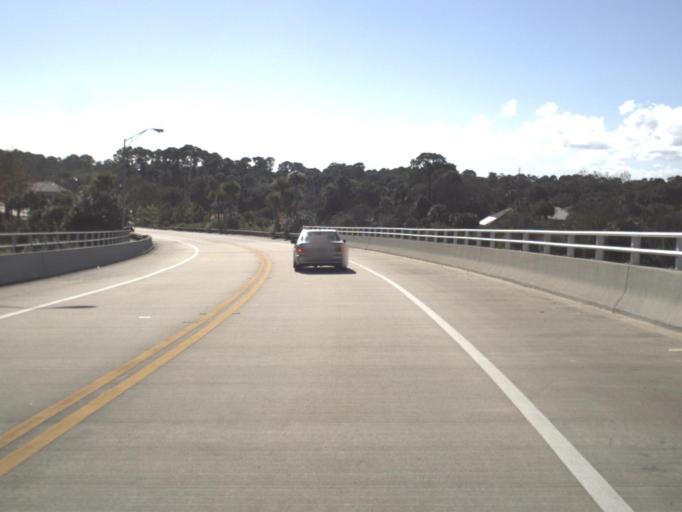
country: US
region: Florida
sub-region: Flagler County
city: Palm Coast
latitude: 29.5719
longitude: -81.1914
